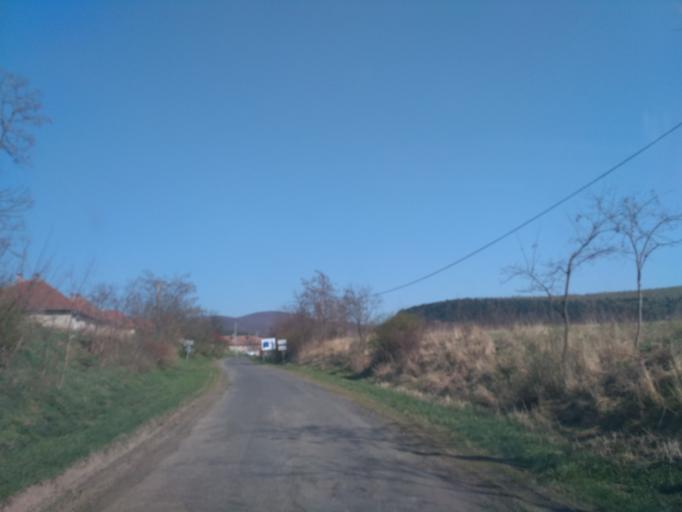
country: HU
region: Borsod-Abauj-Zemplen
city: Gonc
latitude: 48.5317
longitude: 21.3409
